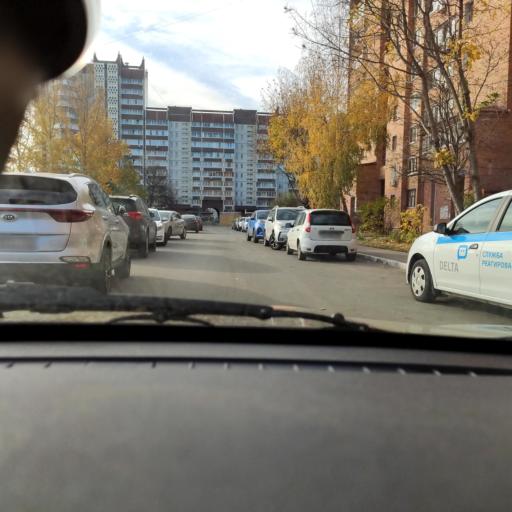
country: RU
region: Samara
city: Tol'yatti
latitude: 53.5057
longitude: 49.2986
